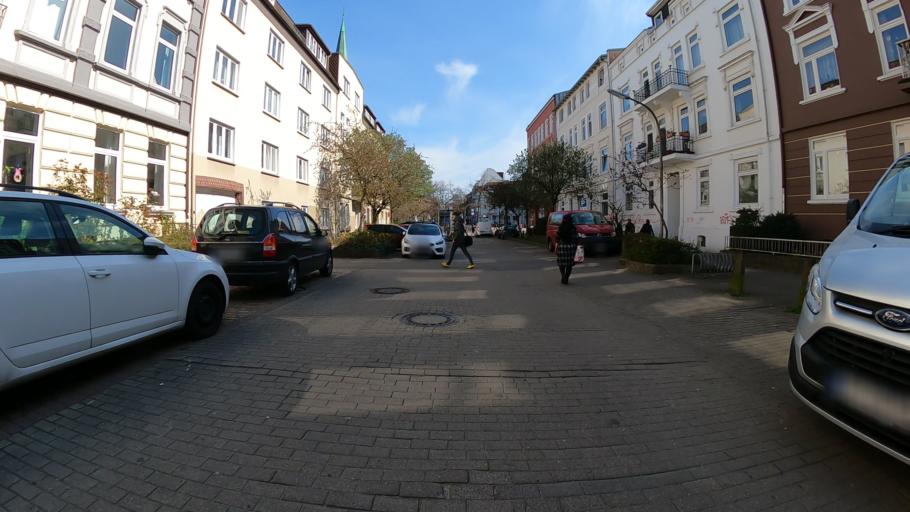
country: DE
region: Hamburg
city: Harburg
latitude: 53.4660
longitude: 9.9618
